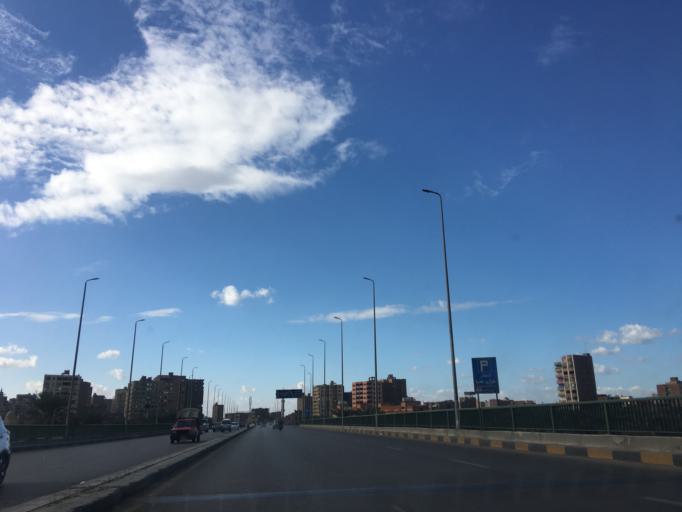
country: EG
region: Al Jizah
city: Al Jizah
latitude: 30.0292
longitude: 31.1910
